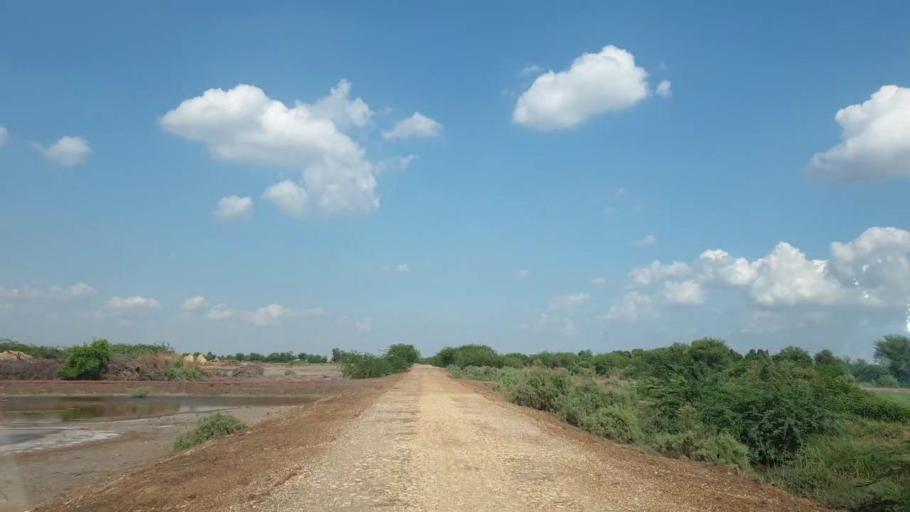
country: PK
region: Sindh
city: Pithoro
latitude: 25.5987
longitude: 69.3996
